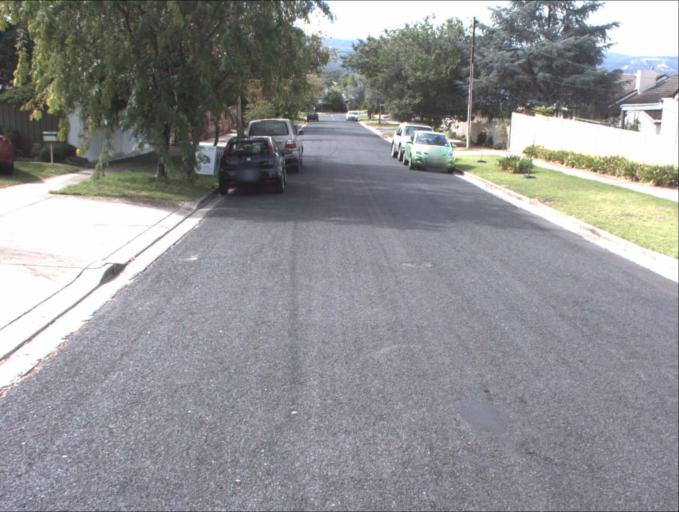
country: AU
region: South Australia
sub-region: Port Adelaide Enfield
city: Klemzig
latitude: -34.8795
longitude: 138.6314
